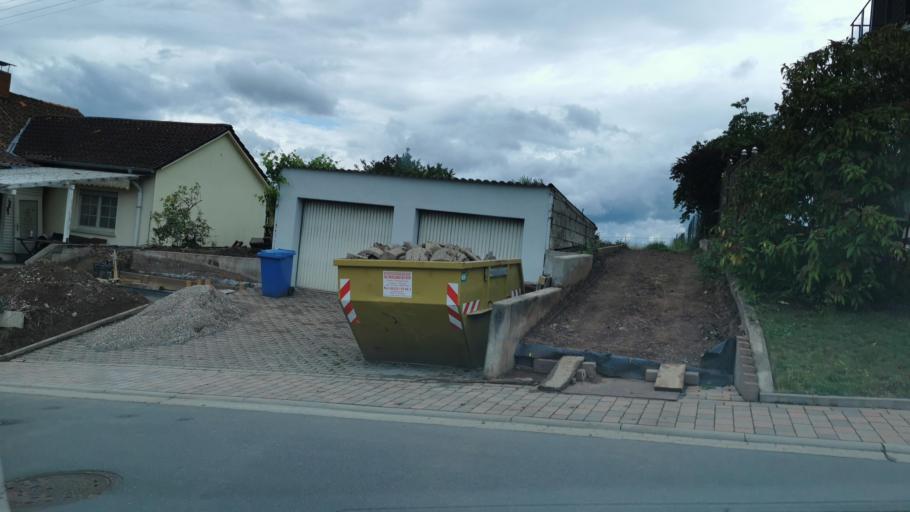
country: DE
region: Rheinland-Pfalz
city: Battweiler
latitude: 49.2788
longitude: 7.4593
